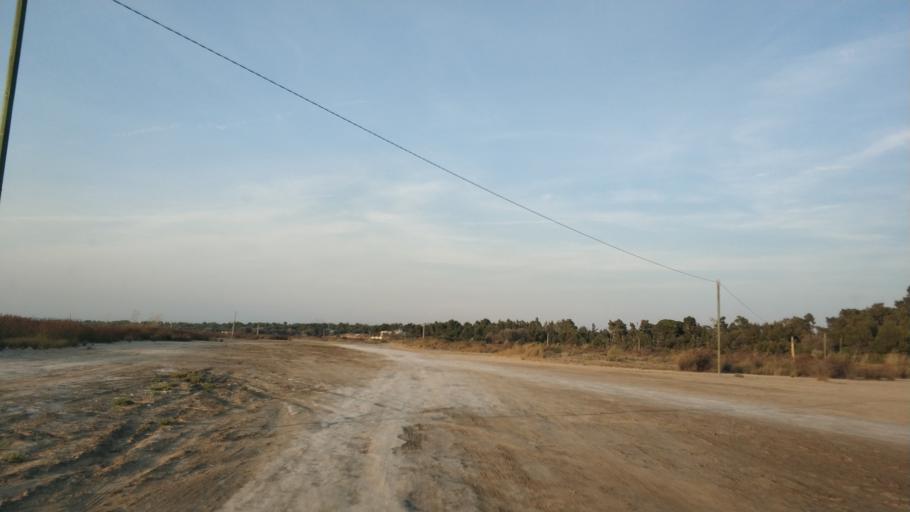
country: AL
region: Fier
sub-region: Rrethi i Lushnjes
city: Divjake
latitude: 40.9644
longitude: 19.4742
